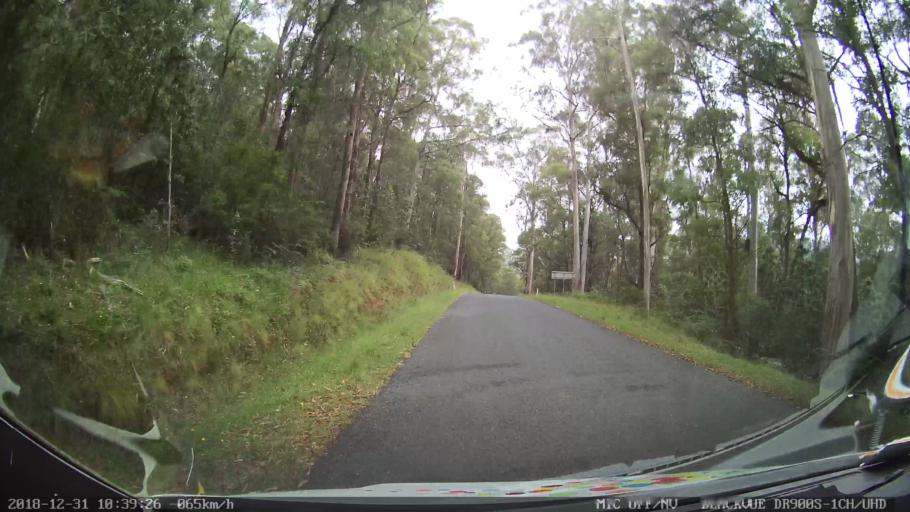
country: AU
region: New South Wales
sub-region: Snowy River
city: Jindabyne
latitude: -36.3991
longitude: 148.1768
